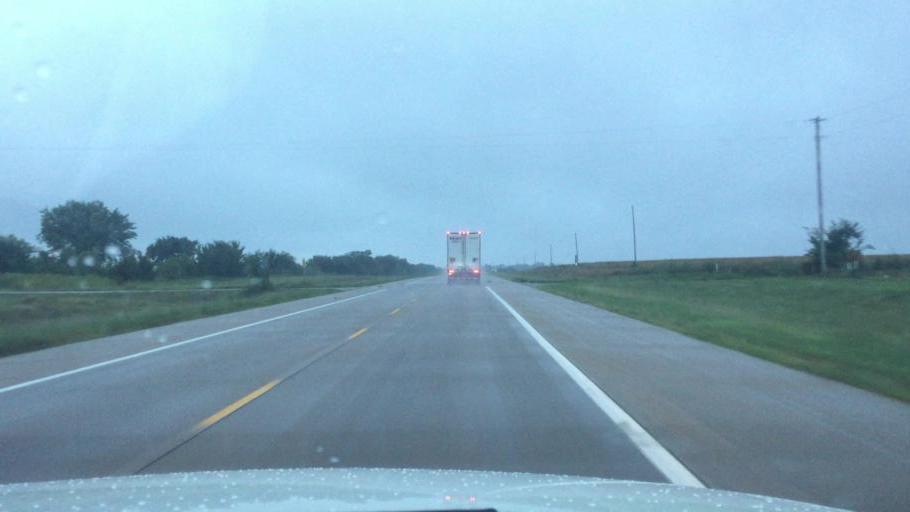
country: US
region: Kansas
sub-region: Neosho County
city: Chanute
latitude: 37.5150
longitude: -95.4709
